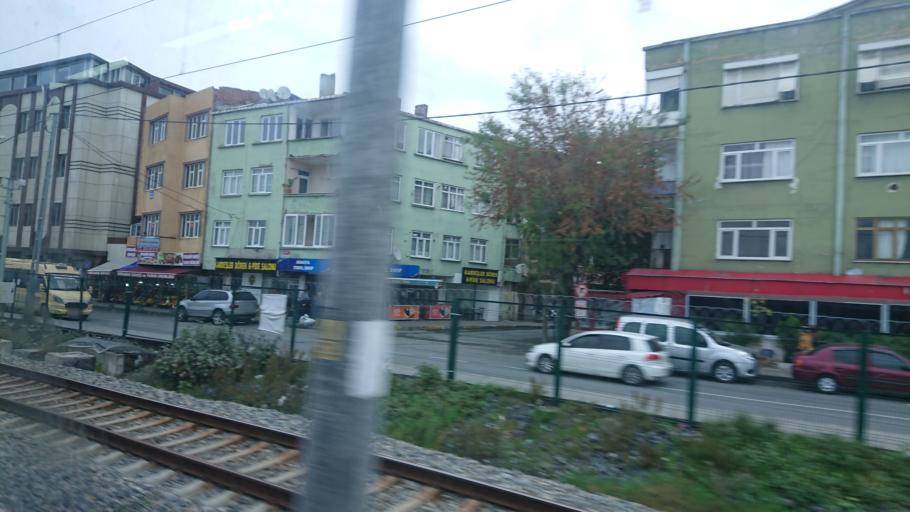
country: TR
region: Istanbul
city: Mahmutbey
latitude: 41.0087
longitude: 28.7747
